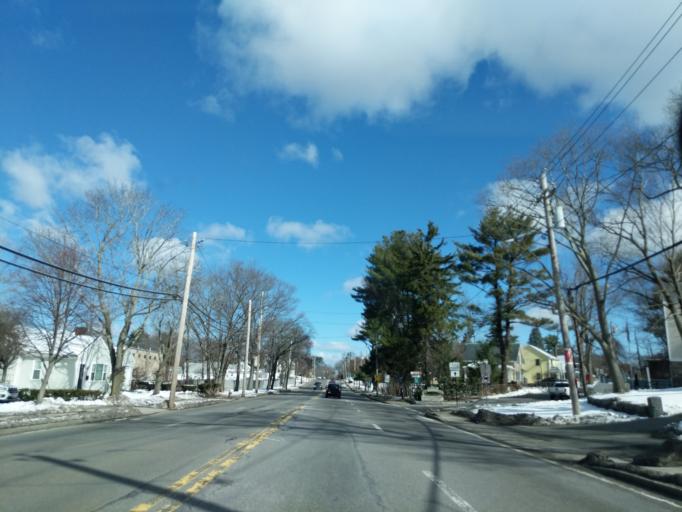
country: US
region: Massachusetts
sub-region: Norfolk County
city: Milton
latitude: 42.2451
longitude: -71.0693
